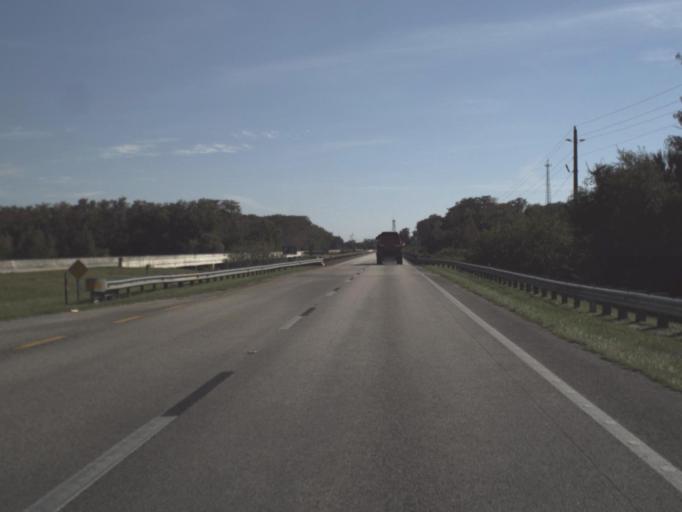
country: US
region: Florida
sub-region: Hendry County
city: Port LaBelle
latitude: 26.9345
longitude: -81.3158
